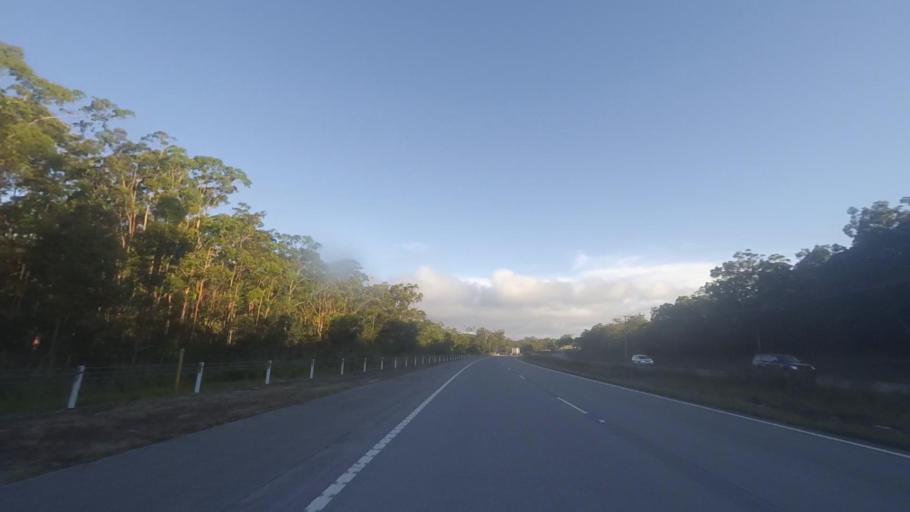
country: AU
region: New South Wales
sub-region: Great Lakes
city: Bulahdelah
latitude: -32.4990
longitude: 152.2084
